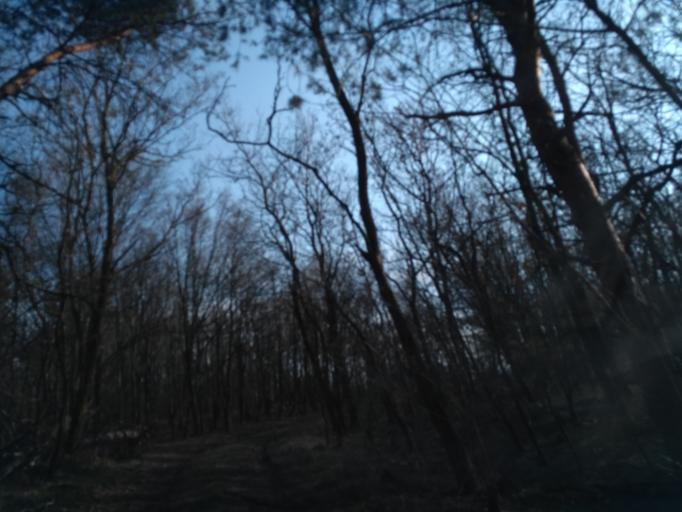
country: HU
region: Borsod-Abauj-Zemplen
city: Satoraljaujhely
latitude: 48.4302
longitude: 21.7091
